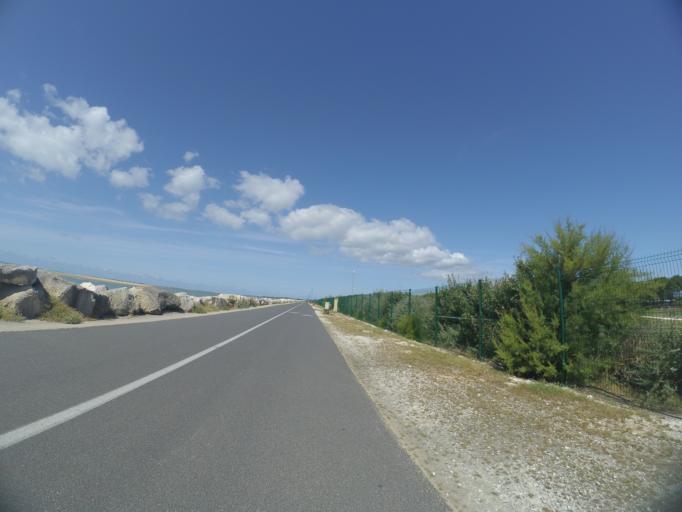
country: FR
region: Poitou-Charentes
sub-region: Departement de la Charente-Maritime
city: Les Mathes
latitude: 45.6756
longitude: -1.1666
